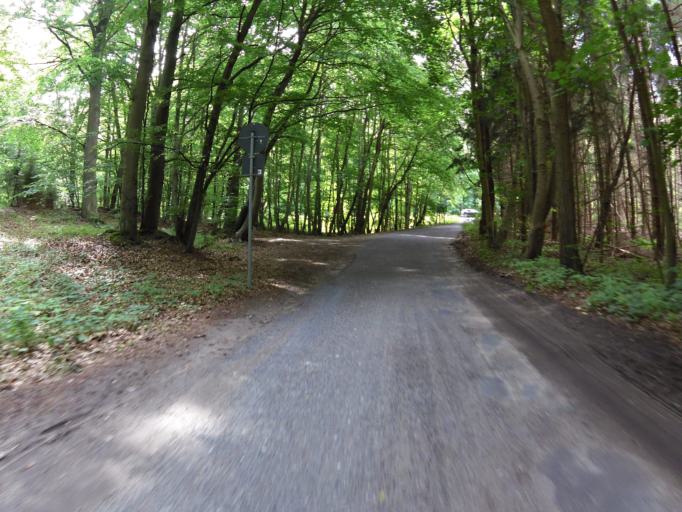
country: DE
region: Mecklenburg-Vorpommern
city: Seebad Bansin
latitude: 53.9771
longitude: 14.1072
